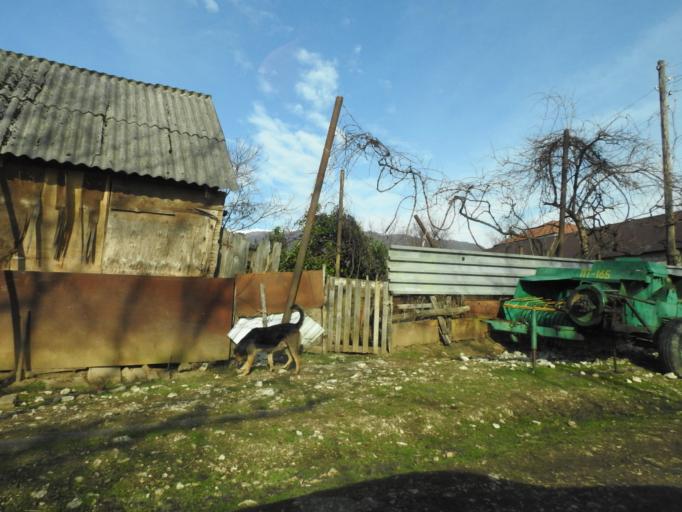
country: GE
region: Abkhazia
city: Gudauta
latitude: 43.2041
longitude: 40.6463
